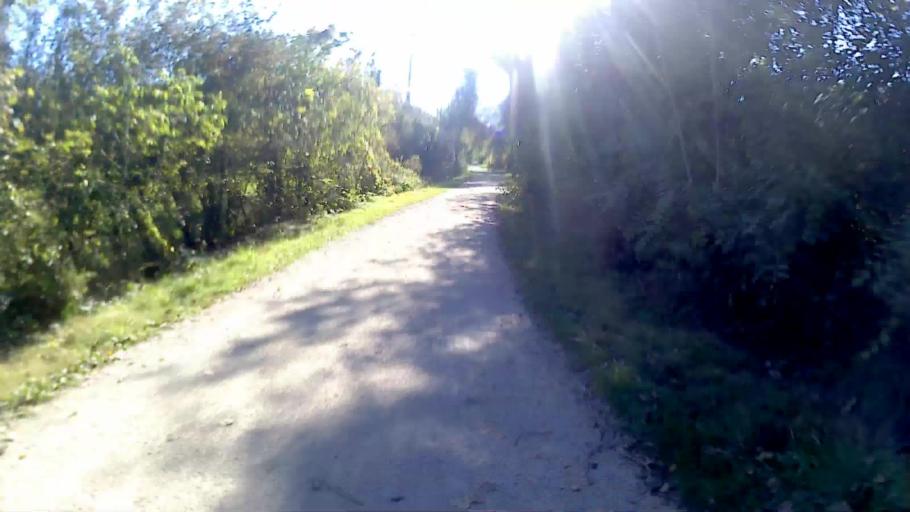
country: US
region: Illinois
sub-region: DuPage County
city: Glen Ellyn
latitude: 41.8725
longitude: -88.0839
